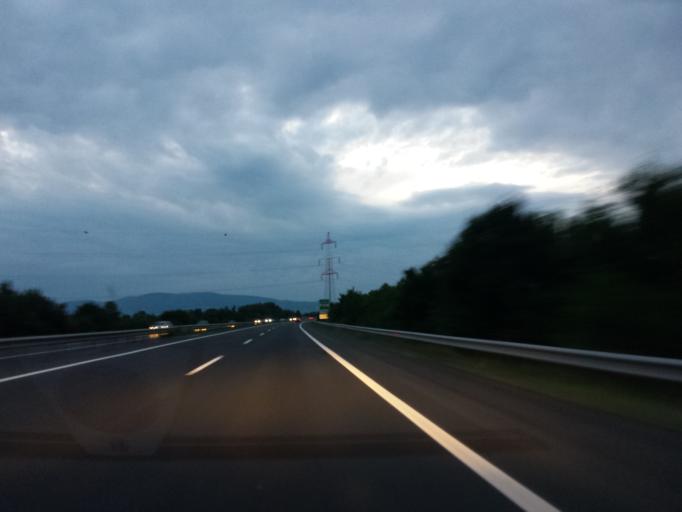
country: AT
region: Lower Austria
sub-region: Politischer Bezirk Modling
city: Munchendorf
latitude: 48.0095
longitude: 16.3736
